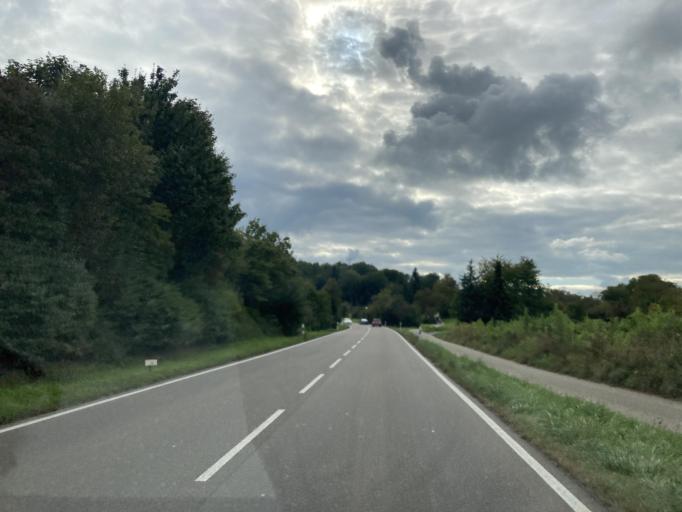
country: DE
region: Baden-Wuerttemberg
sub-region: Karlsruhe Region
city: Birkenfeld
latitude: 48.8687
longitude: 8.6228
